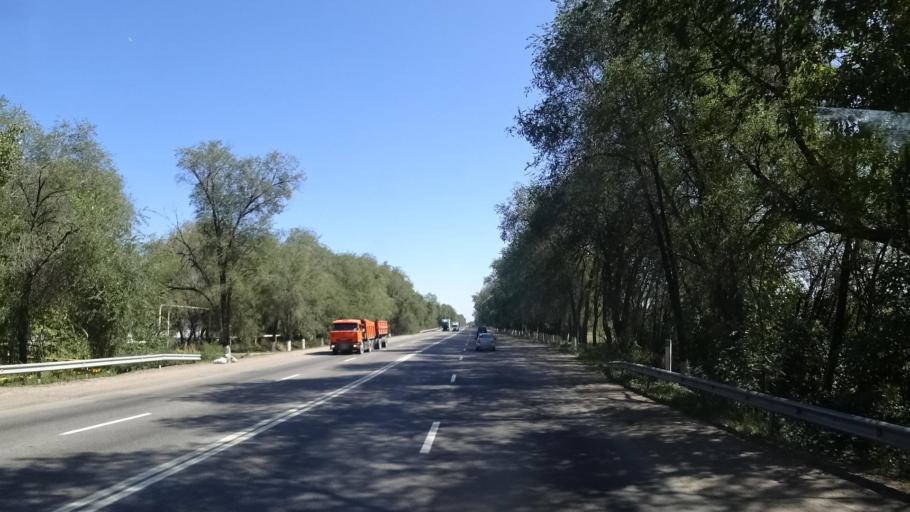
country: KZ
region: Almaty Oblysy
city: Energeticheskiy
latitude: 43.3951
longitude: 77.1427
